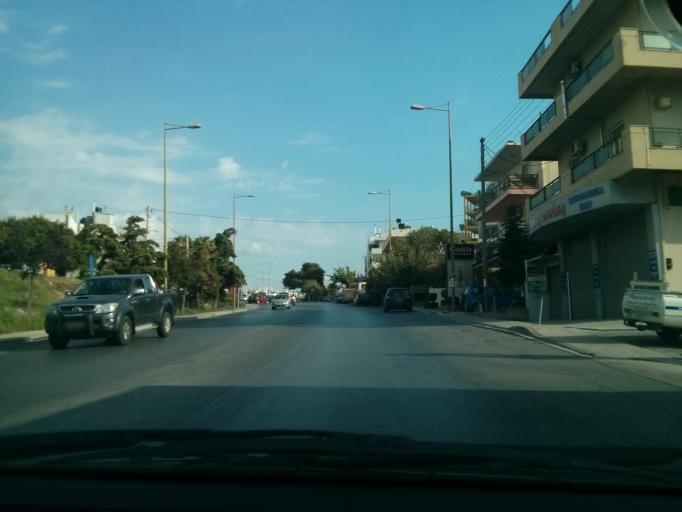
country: GR
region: Crete
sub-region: Nomos Irakleiou
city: Irakleion
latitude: 35.3242
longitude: 25.1402
